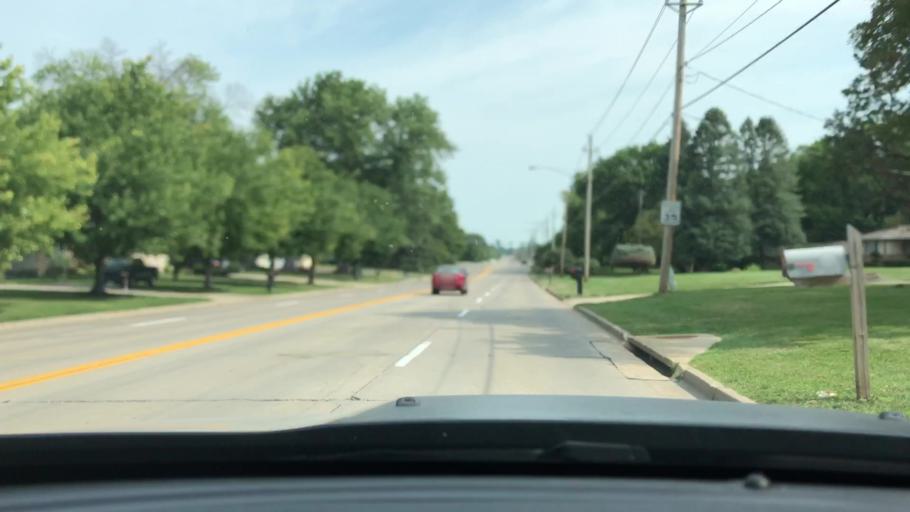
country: US
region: Iowa
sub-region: Scott County
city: Bettendorf
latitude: 41.5652
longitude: -90.5416
